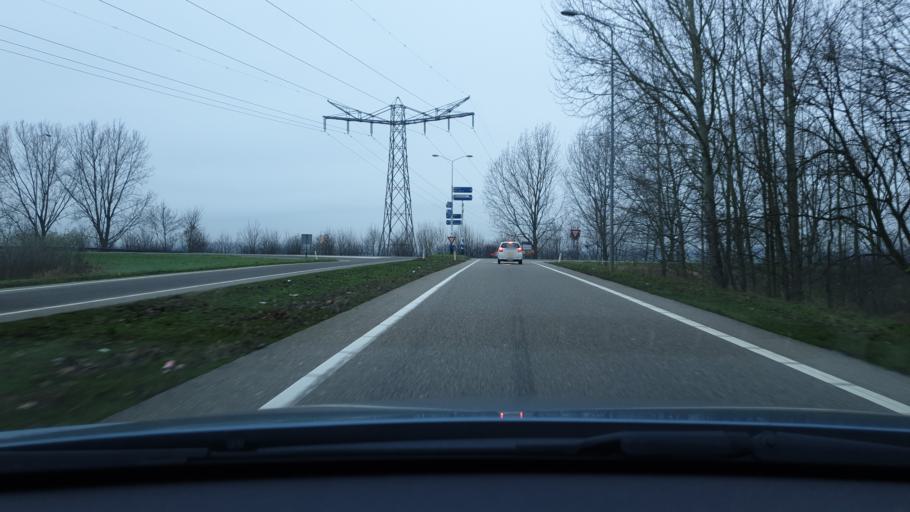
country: NL
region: Gelderland
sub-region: Gemeente Wijchen
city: Bergharen
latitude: 51.8734
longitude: 5.6615
